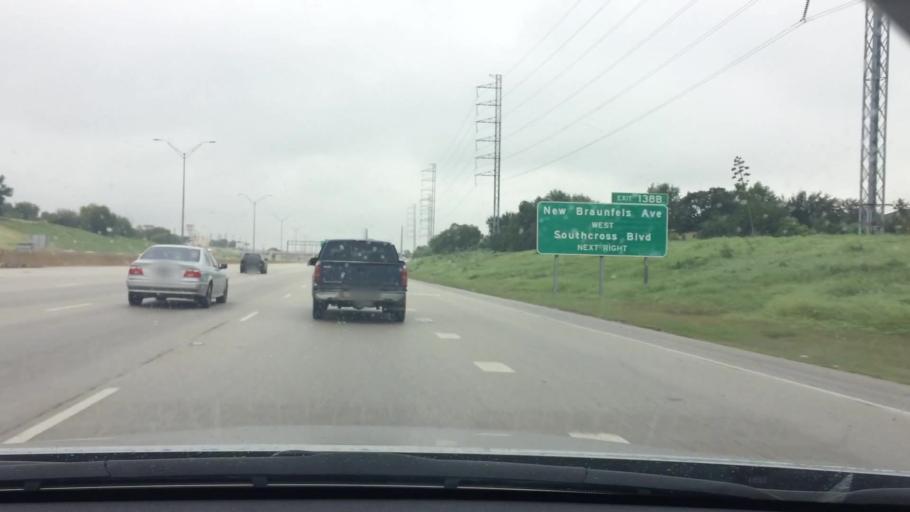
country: US
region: Texas
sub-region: Bexar County
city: San Antonio
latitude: 29.3804
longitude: -98.4658
